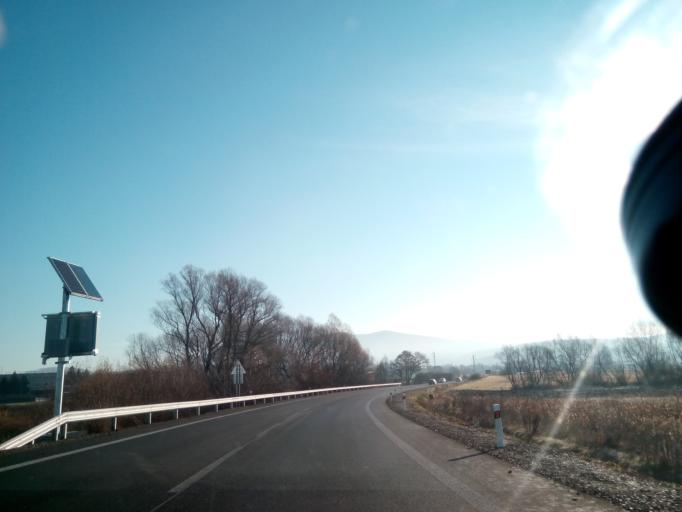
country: SK
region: Kosicky
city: Kosice
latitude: 48.7363
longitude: 21.4302
